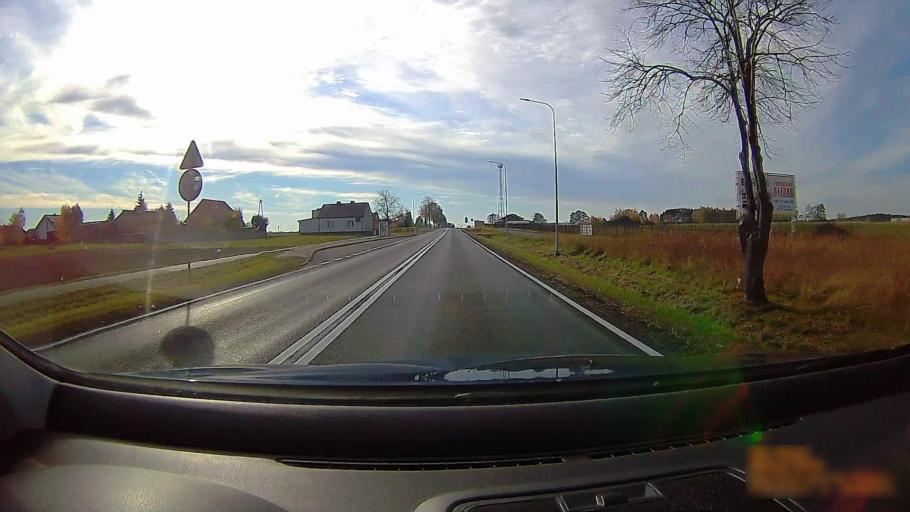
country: PL
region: Greater Poland Voivodeship
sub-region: Powiat koninski
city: Rychwal
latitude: 52.0579
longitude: 18.1635
